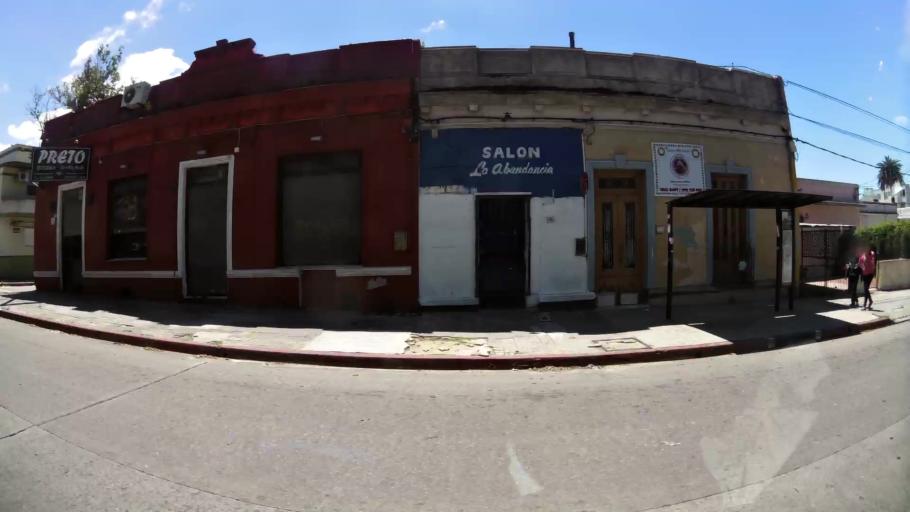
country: UY
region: Montevideo
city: Montevideo
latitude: -34.8938
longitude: -56.1235
